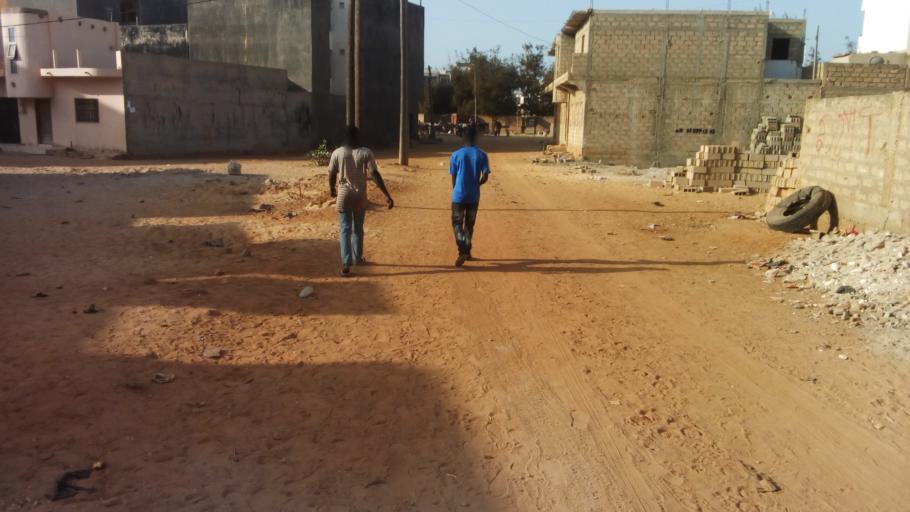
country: SN
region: Dakar
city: Pikine
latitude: 14.8029
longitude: -17.3396
